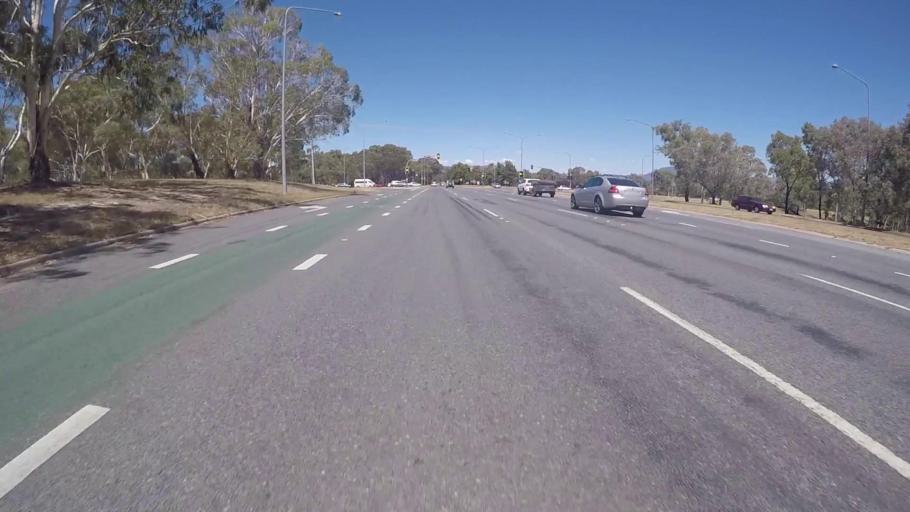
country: AU
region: Australian Capital Territory
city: Macarthur
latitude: -35.3954
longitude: 149.0718
